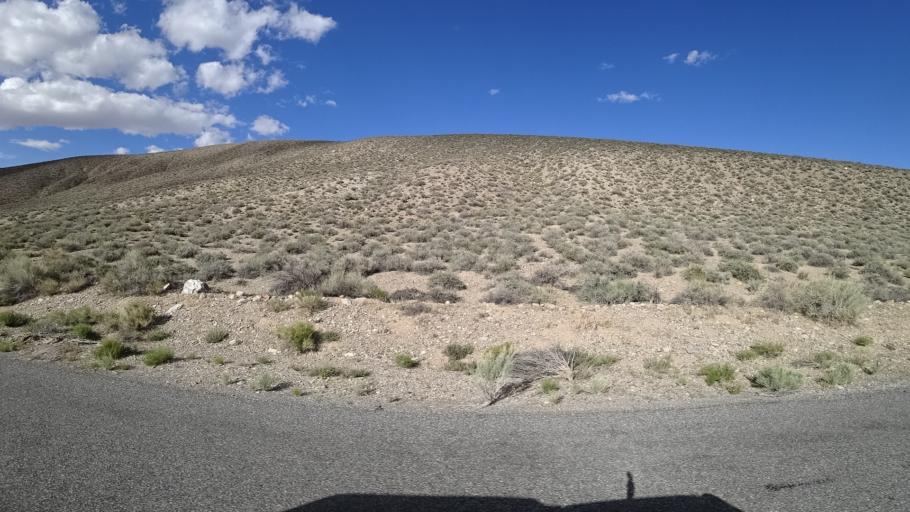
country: US
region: Nevada
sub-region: Nye County
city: Beatty
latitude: 36.3914
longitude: -117.1549
